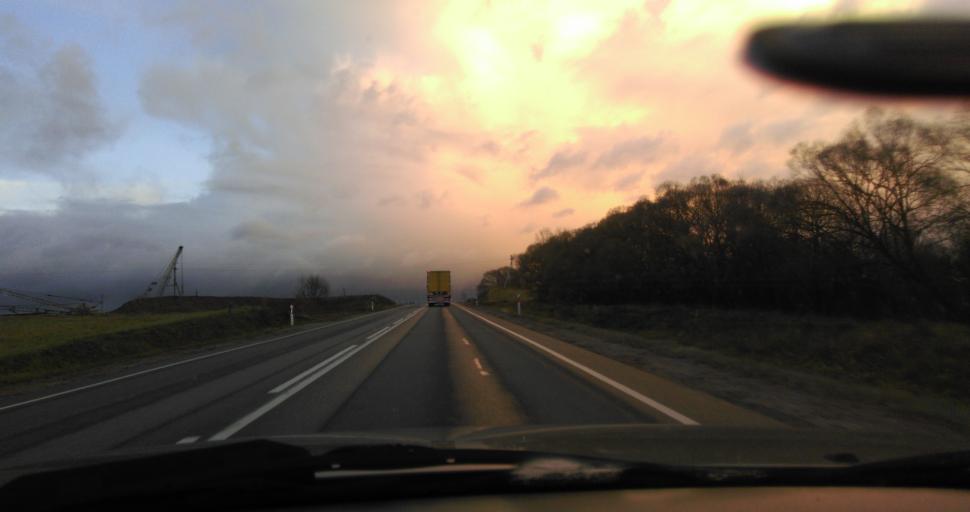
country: LT
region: Utenos apskritis
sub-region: Utena
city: Utena
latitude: 55.5194
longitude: 25.6607
